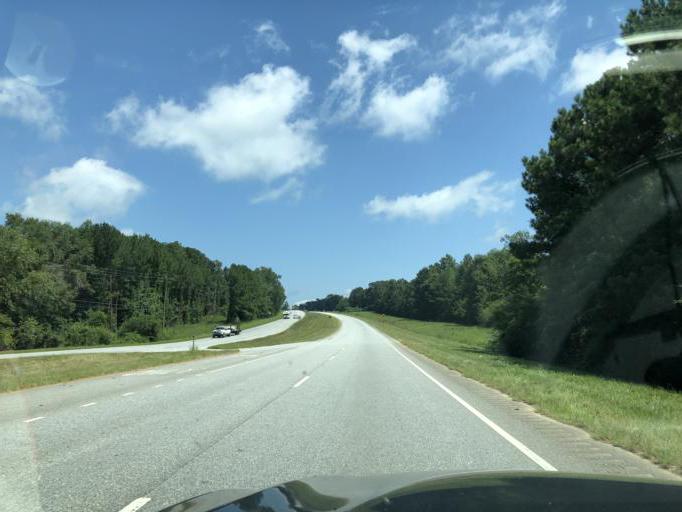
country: US
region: Alabama
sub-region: Barbour County
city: Eufaula
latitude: 31.7725
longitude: -85.1836
